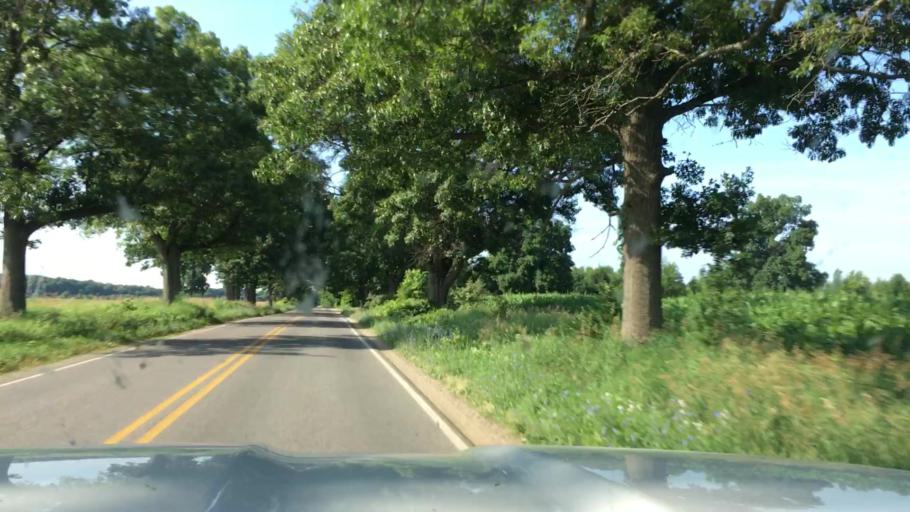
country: US
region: Michigan
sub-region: Barry County
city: Stony Point
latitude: 42.4490
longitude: -85.4544
